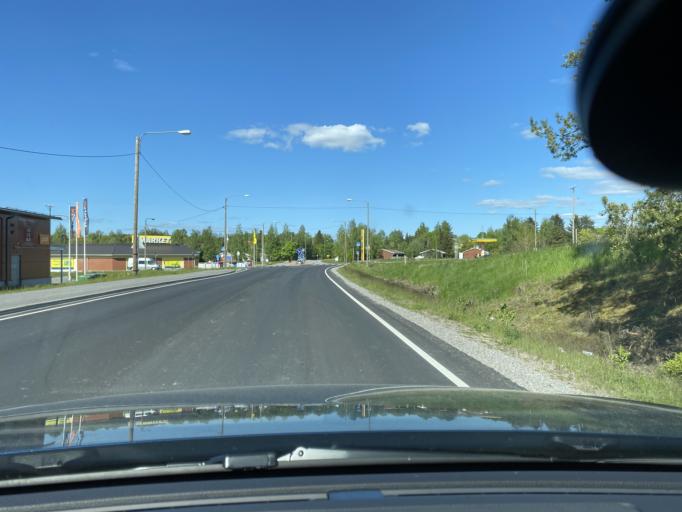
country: FI
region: Varsinais-Suomi
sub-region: Turku
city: Sauvo
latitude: 60.3411
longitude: 22.6872
